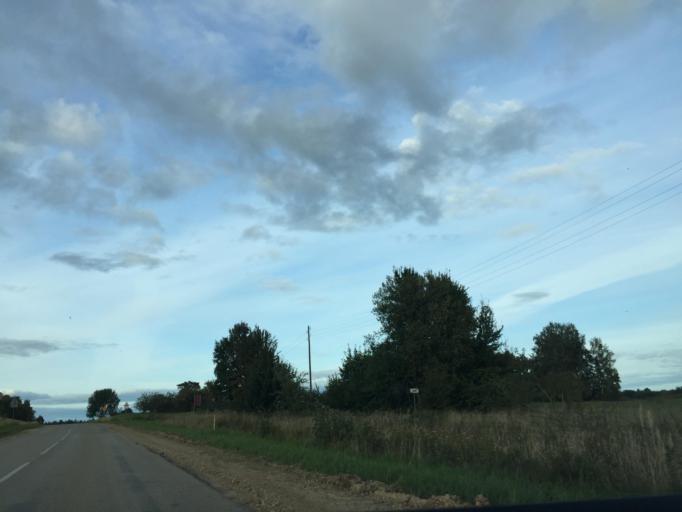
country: LV
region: Nereta
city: Nereta
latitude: 56.2870
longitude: 25.4090
